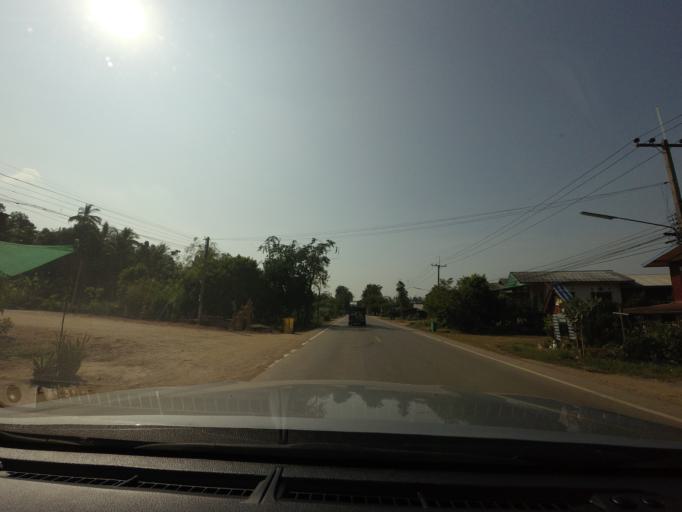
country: TH
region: Sukhothai
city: Kong Krailat
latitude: 16.8527
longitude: 99.9555
